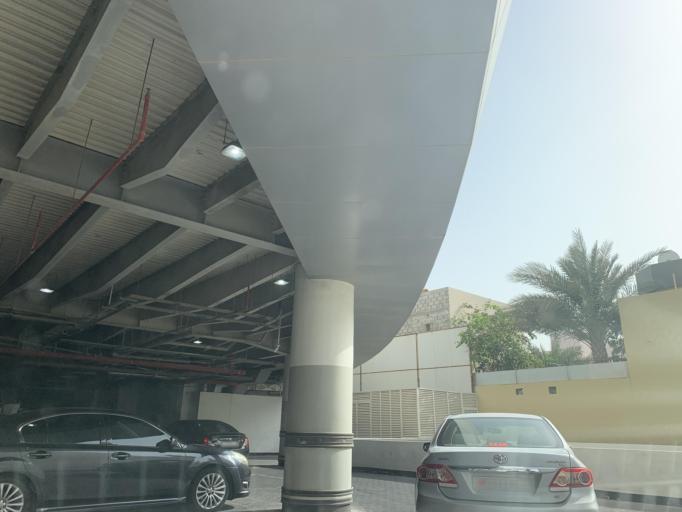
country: BH
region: Northern
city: Ar Rifa'
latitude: 26.1308
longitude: 50.5736
